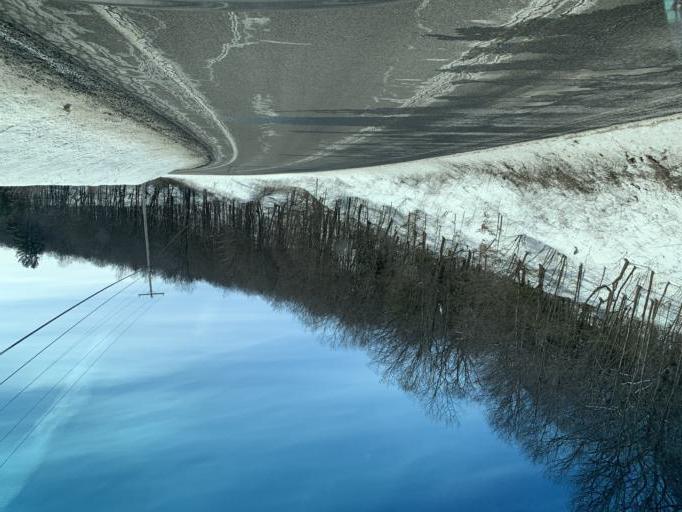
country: US
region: Maryland
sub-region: Allegany County
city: Lonaconing
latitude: 39.5955
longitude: -78.9433
